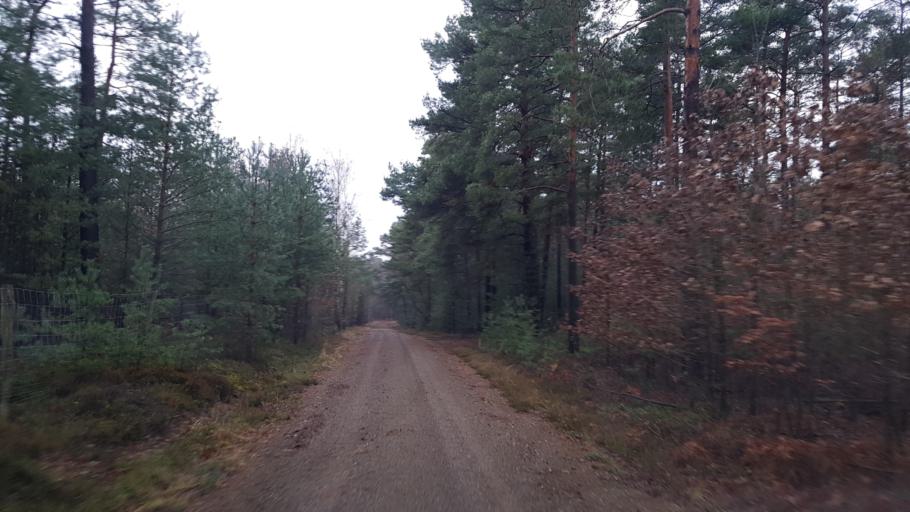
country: DE
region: Brandenburg
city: Bronkow
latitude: 51.6340
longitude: 13.9554
